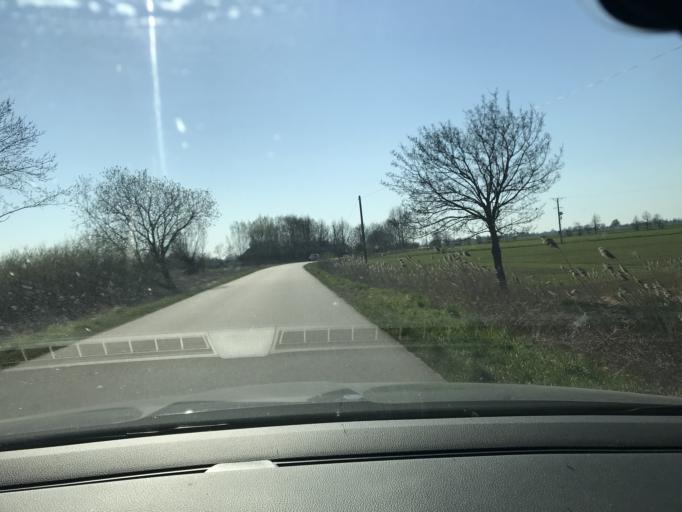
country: PL
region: Pomeranian Voivodeship
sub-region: Powiat nowodworski
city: Stegna
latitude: 54.2973
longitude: 19.1398
